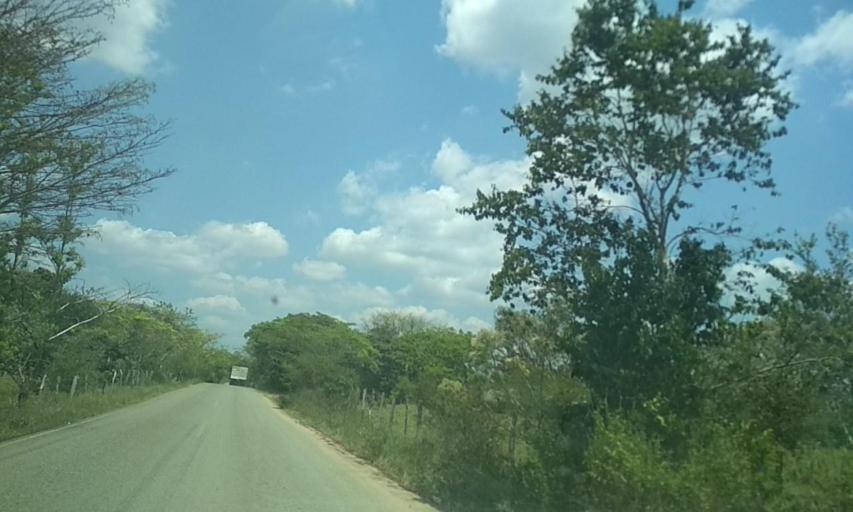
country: MX
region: Tabasco
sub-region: Huimanguillo
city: Francisco Rueda
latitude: 17.7735
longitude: -93.8105
